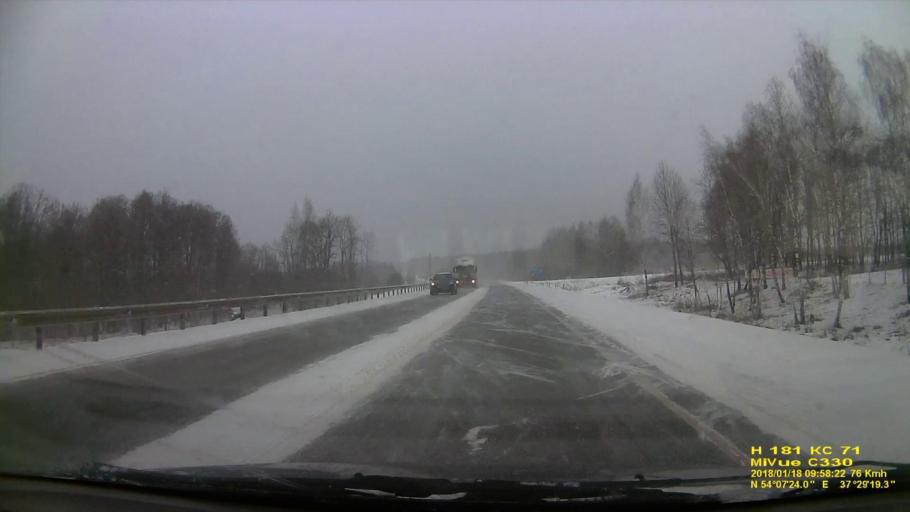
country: RU
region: Tula
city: Kosaya Gora
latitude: 54.1232
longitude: 37.4886
